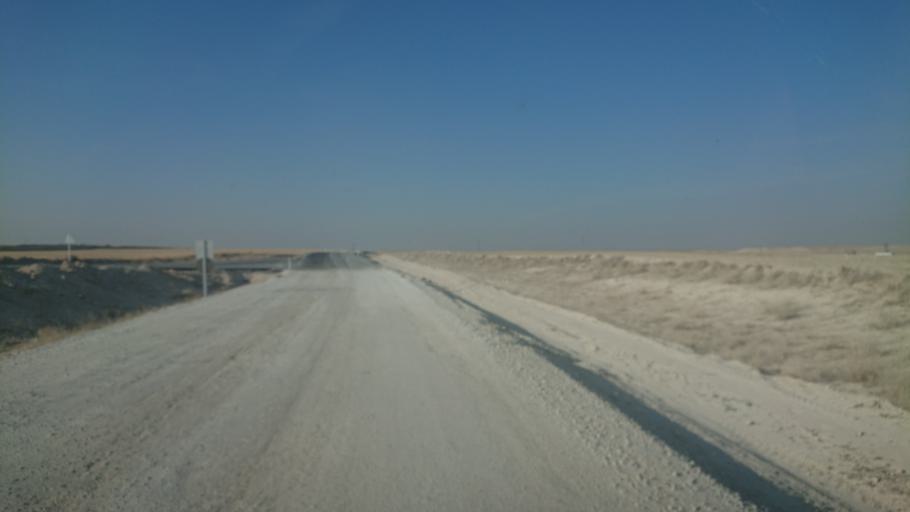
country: TR
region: Aksaray
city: Sultanhani
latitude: 38.0853
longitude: 33.6148
